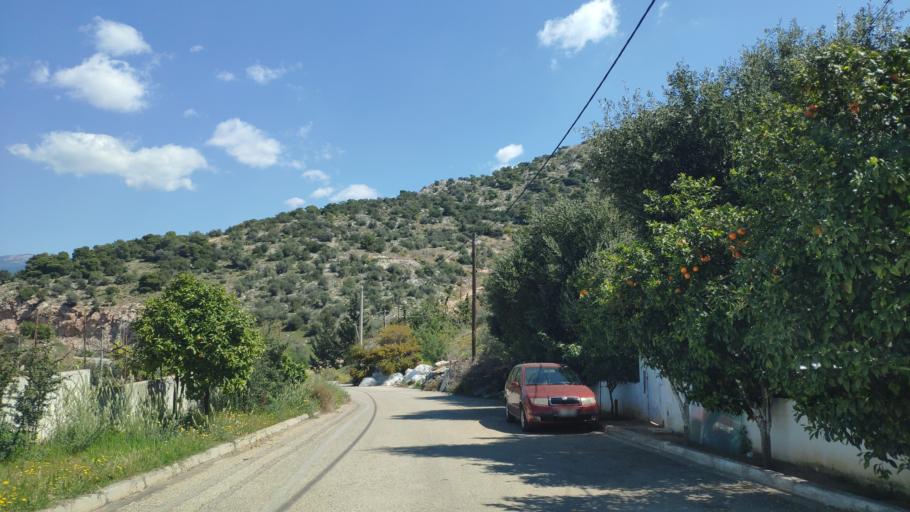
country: GR
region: Attica
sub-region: Nomarchia Athinas
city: Chaidari
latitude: 38.0329
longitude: 23.6366
